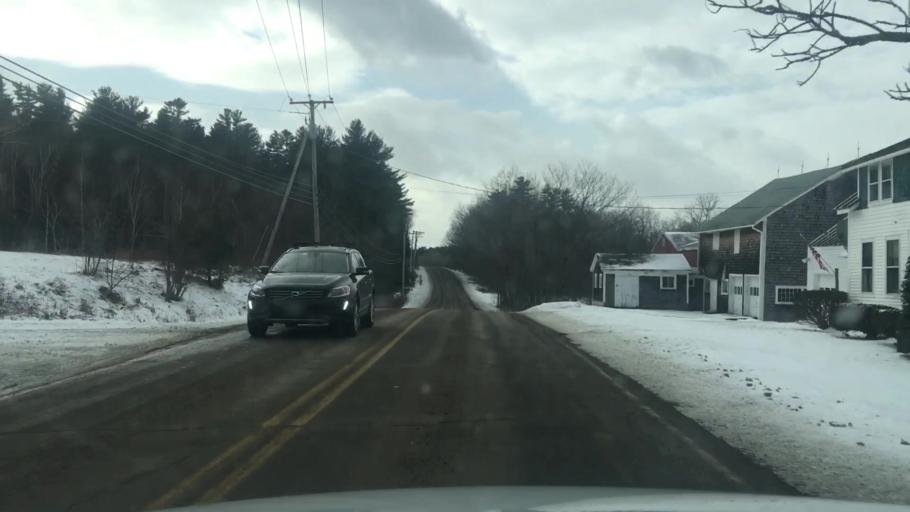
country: US
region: Maine
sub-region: Knox County
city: Hope
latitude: 44.2906
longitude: -69.0910
